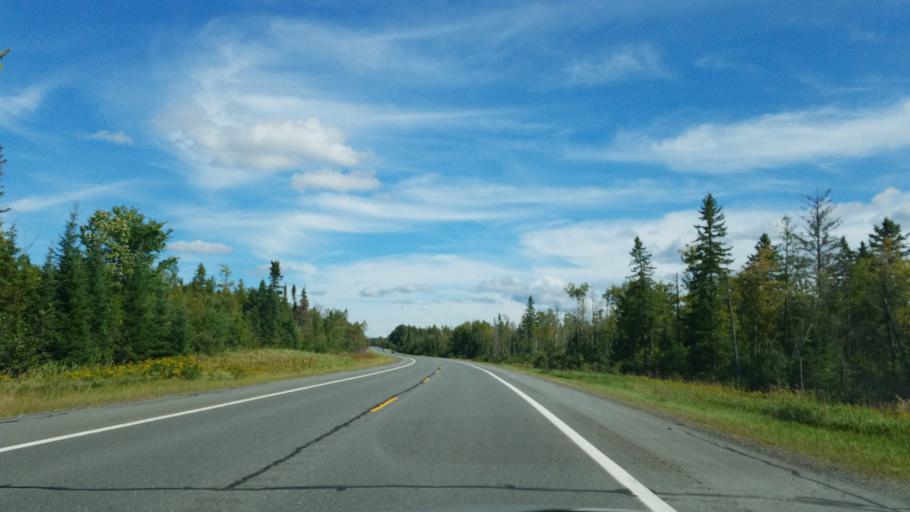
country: US
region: Michigan
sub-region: Baraga County
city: L'Anse
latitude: 46.5819
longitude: -88.4663
